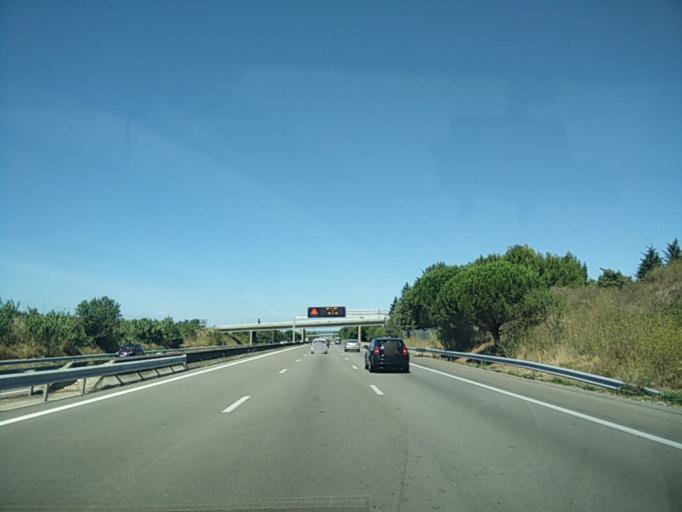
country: FR
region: Provence-Alpes-Cote d'Azur
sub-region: Departement du Vaucluse
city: Morieres-les-Avignon
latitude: 43.9524
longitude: 4.9077
